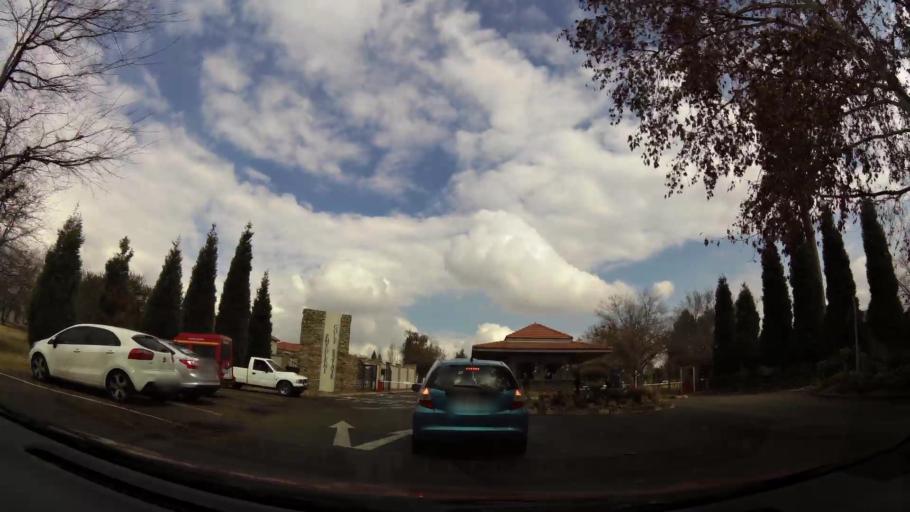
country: ZA
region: Gauteng
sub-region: Sedibeng District Municipality
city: Vanderbijlpark
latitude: -26.7426
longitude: 27.8420
